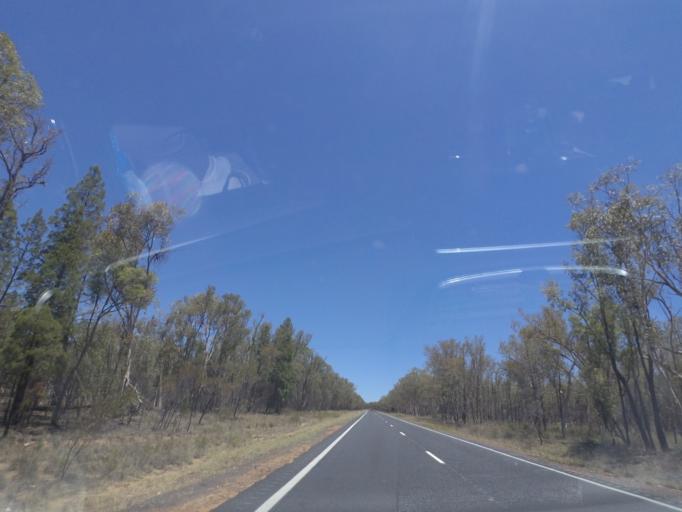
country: AU
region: New South Wales
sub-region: Warrumbungle Shire
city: Coonabarabran
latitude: -31.1724
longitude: 149.3601
